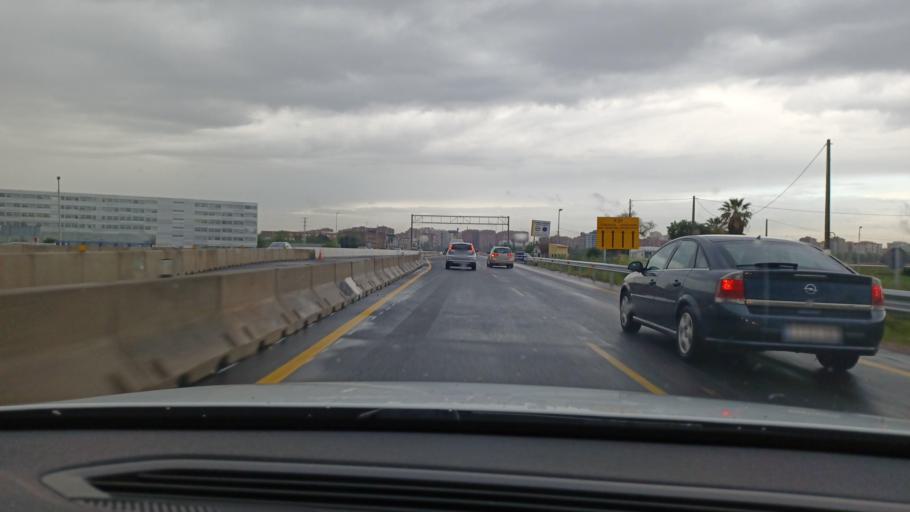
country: ES
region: Valencia
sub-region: Provincia de Valencia
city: Alboraya
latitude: 39.4876
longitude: -0.3422
